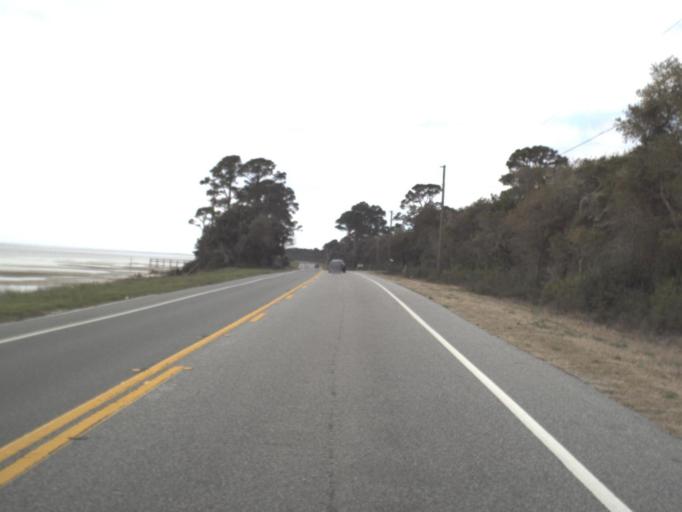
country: US
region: Florida
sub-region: Franklin County
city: Eastpoint
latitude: 29.7797
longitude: -84.7811
